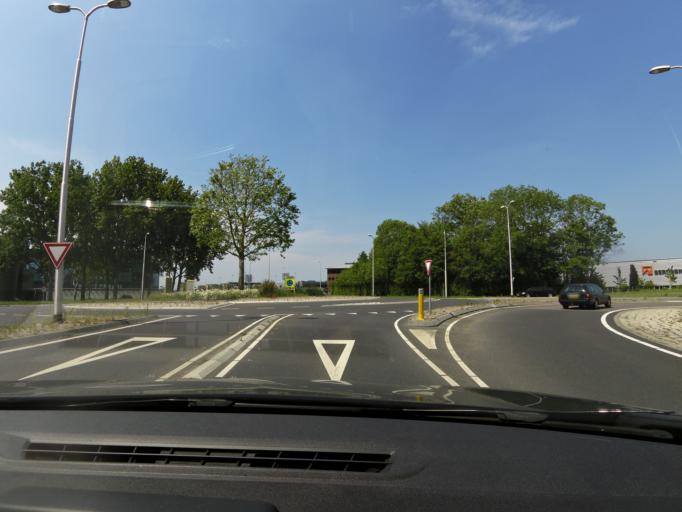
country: NL
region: South Holland
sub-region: Gemeente Lansingerland
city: Bergschenhoek
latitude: 51.9806
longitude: 4.4956
